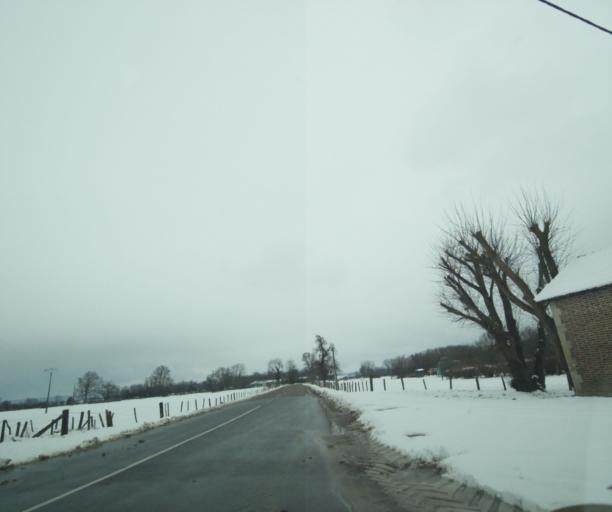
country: FR
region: Champagne-Ardenne
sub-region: Departement de la Haute-Marne
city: Montier-en-Der
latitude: 48.4569
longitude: 4.7694
